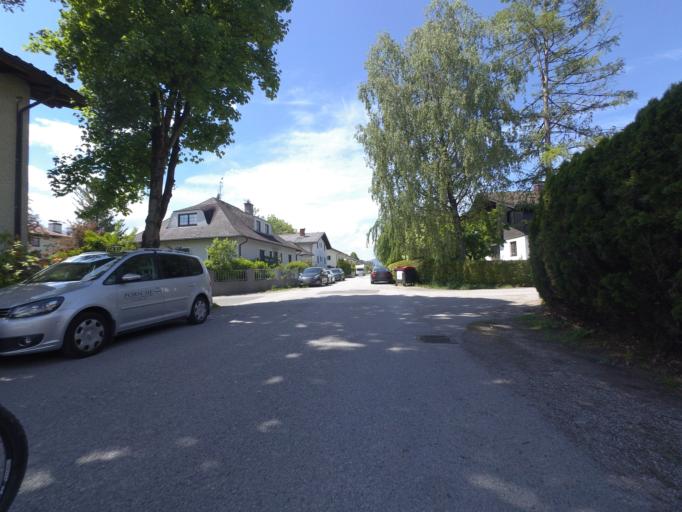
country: AT
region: Salzburg
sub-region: Salzburg Stadt
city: Salzburg
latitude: 47.7747
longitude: 13.0370
